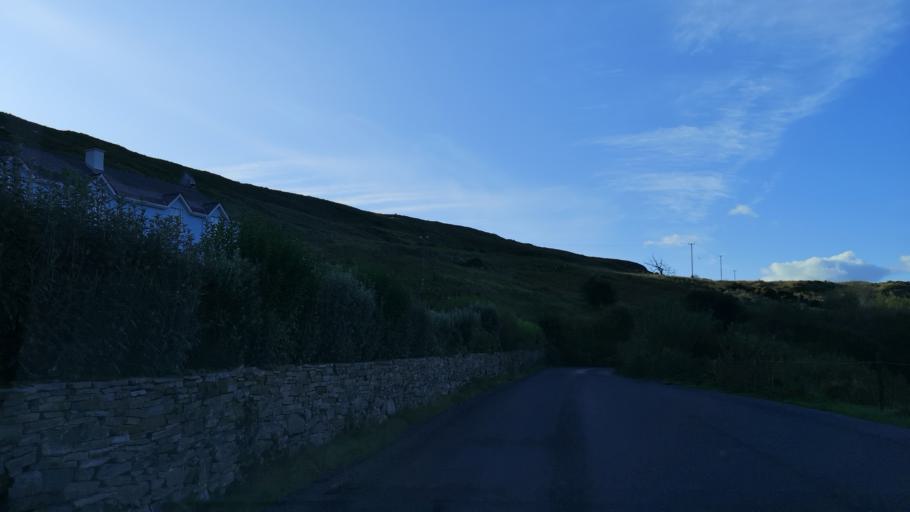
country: IE
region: Connaught
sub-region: County Galway
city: Clifden
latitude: 53.5028
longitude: -10.0610
